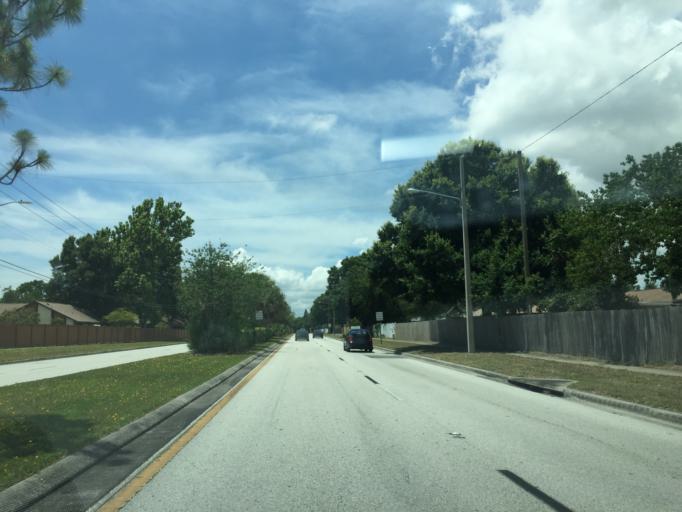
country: US
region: Florida
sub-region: Pinellas County
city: Dunedin
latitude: 28.0155
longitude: -82.7468
